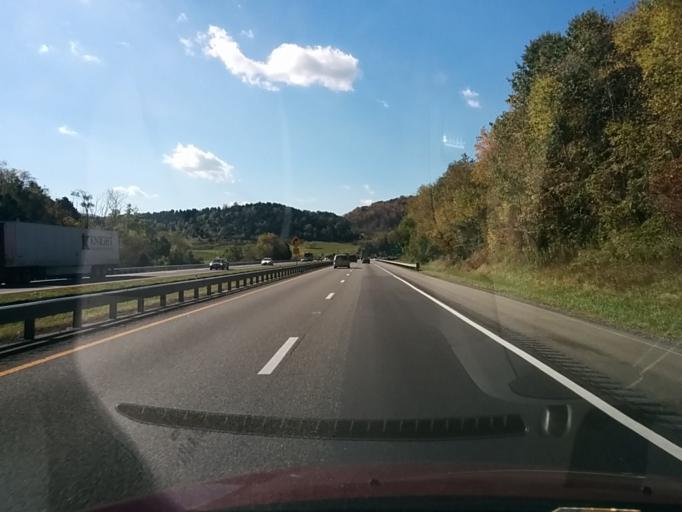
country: US
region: Virginia
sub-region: Botetourt County
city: Buchanan
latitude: 37.5030
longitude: -79.7467
